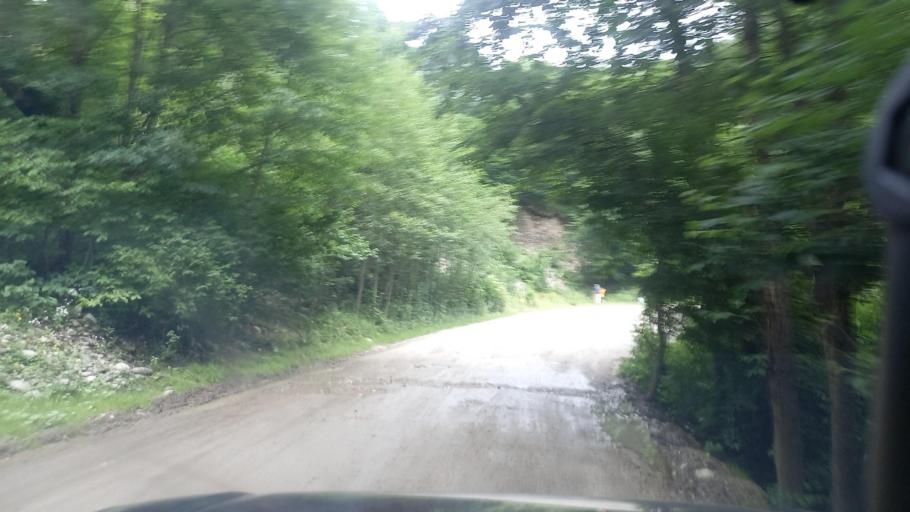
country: RU
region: Karachayevo-Cherkesiya
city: Kurdzhinovo
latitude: 43.8878
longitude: 40.9495
